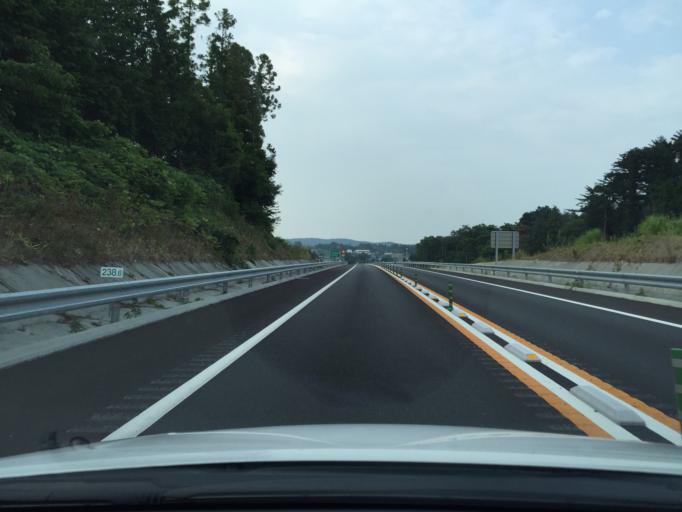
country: JP
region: Fukushima
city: Namie
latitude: 37.5516
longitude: 140.9445
